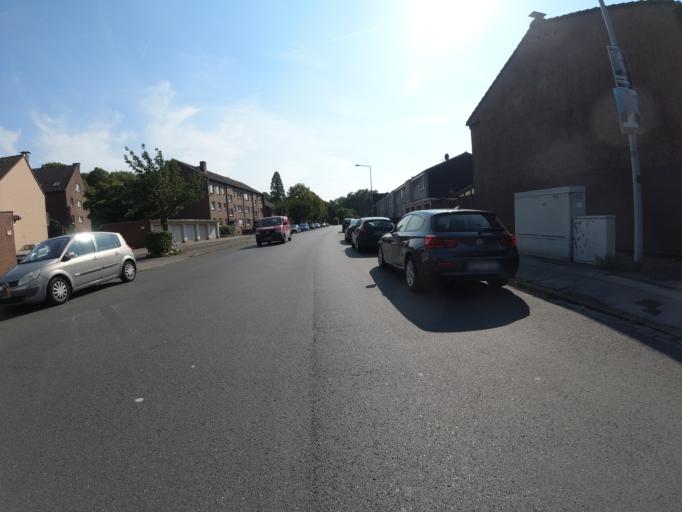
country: DE
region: North Rhine-Westphalia
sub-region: Regierungsbezirk Dusseldorf
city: Hochfeld
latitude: 51.4147
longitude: 6.6979
